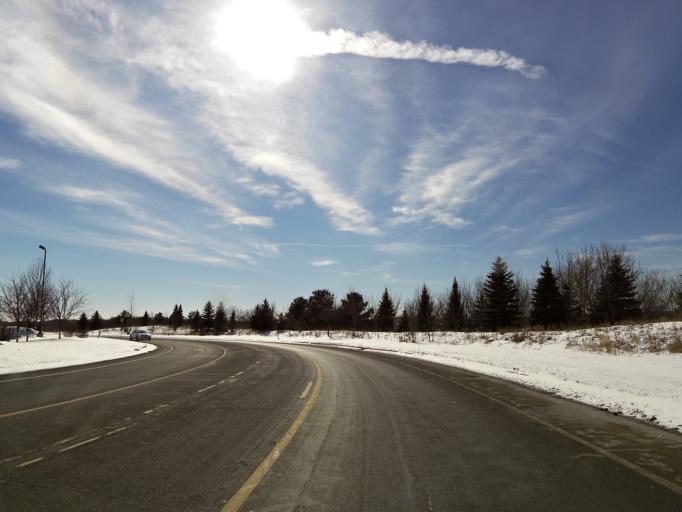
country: US
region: Minnesota
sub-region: Washington County
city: Woodbury
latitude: 44.9413
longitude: -92.9147
